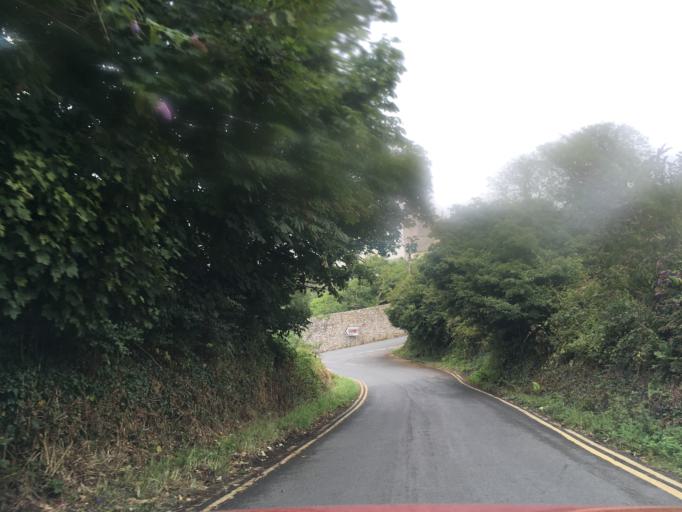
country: GB
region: Wales
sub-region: Pembrokeshire
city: Saint David's
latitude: 51.8804
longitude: -5.2706
